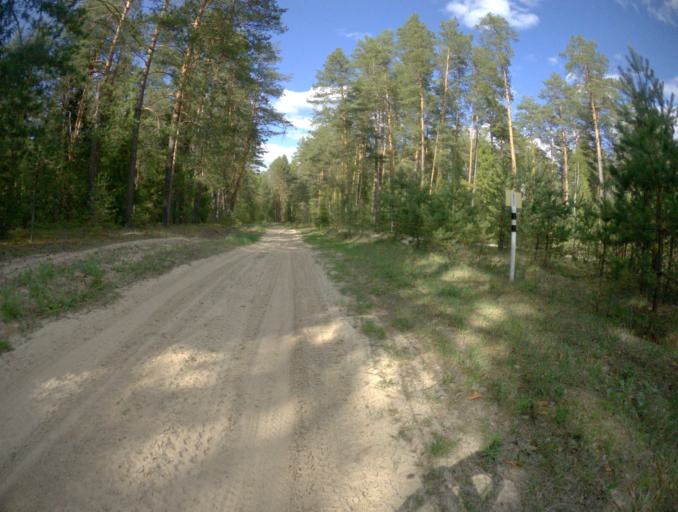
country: RU
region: Vladimir
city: Golovino
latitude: 55.9051
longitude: 40.4415
